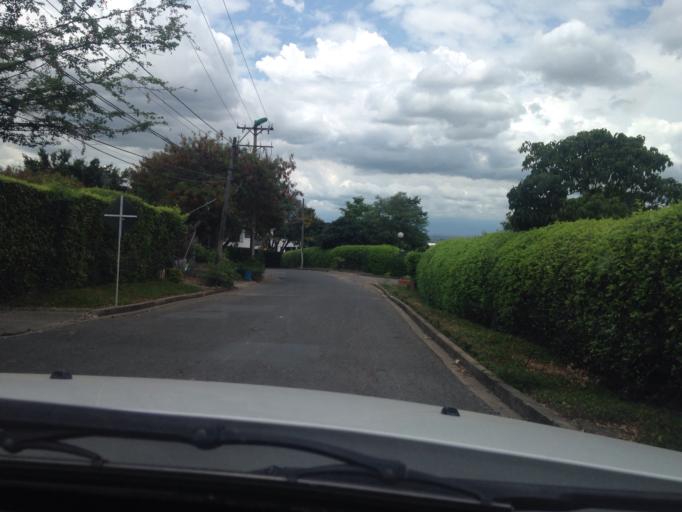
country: CO
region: Valle del Cauca
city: Cali
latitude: 3.4907
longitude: -76.5259
